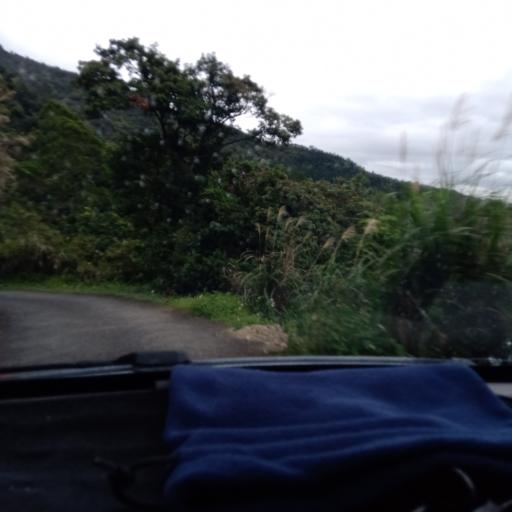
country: TW
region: Taiwan
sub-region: Yilan
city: Yilan
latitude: 24.8092
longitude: 121.6971
